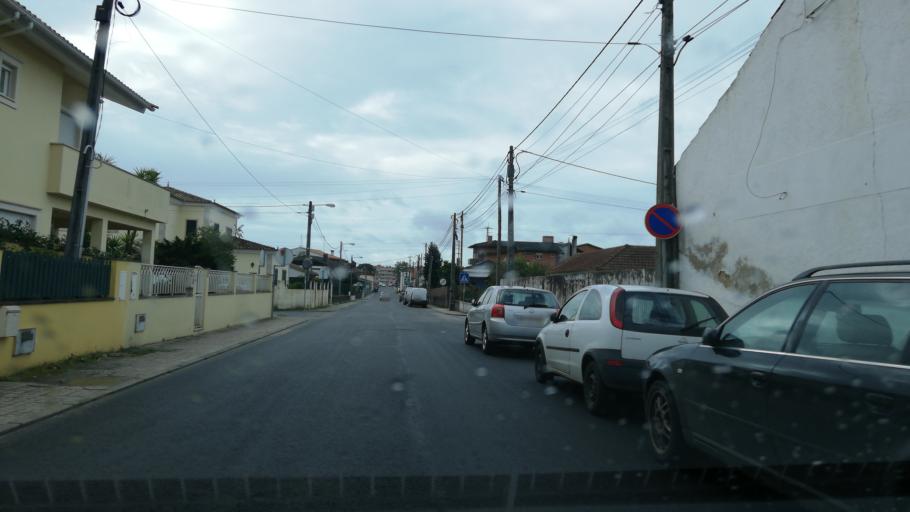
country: PT
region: Aveiro
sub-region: Agueda
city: Agueda
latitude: 40.5946
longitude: -8.4511
